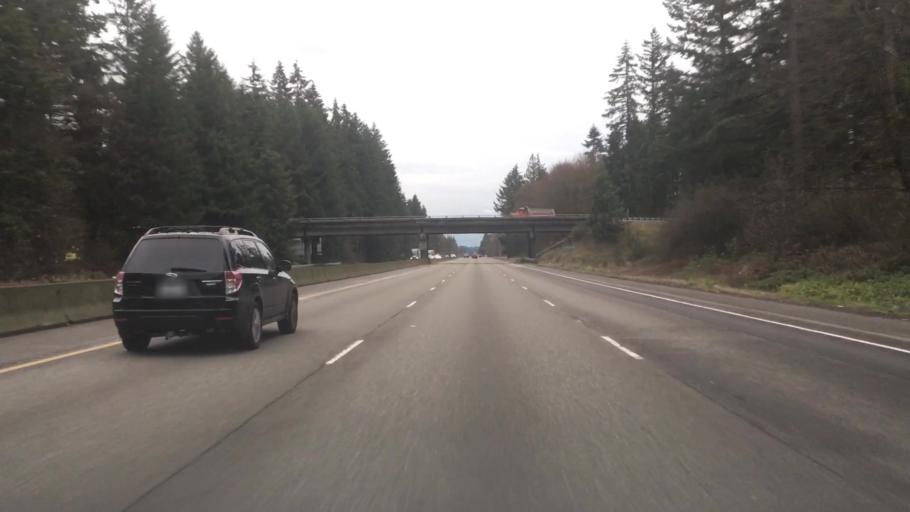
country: US
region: Washington
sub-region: Thurston County
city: Tumwater
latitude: 46.9540
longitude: -122.9373
